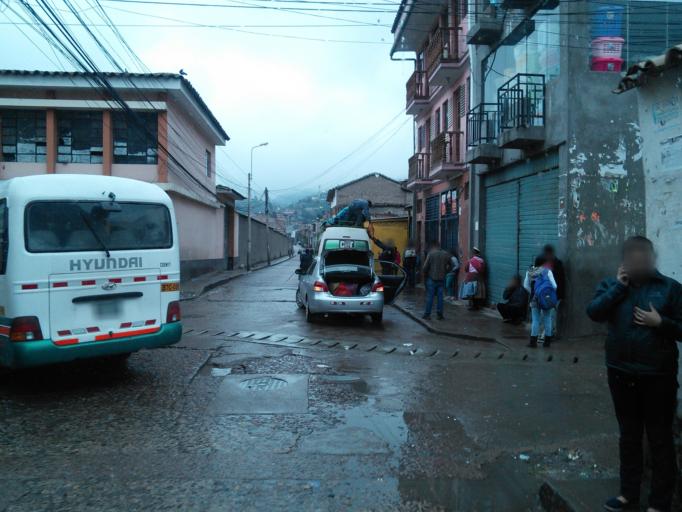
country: PE
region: Ayacucho
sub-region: Provincia de Huamanga
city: Ayacucho
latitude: -13.1625
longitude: -74.2293
